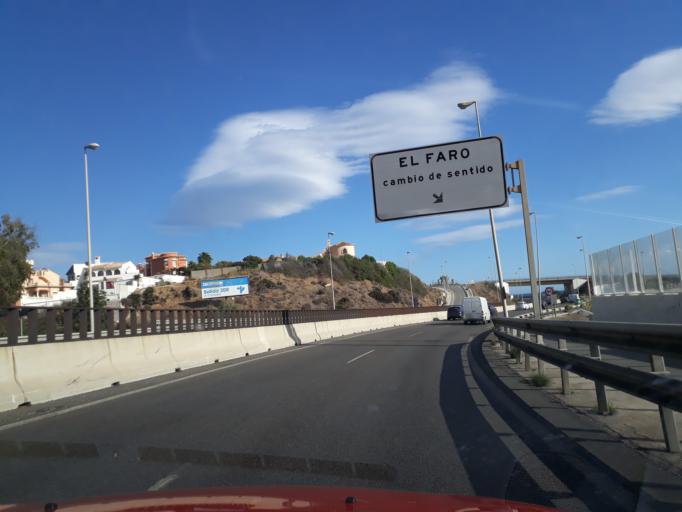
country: ES
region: Andalusia
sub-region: Provincia de Malaga
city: Fuengirola
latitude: 36.5080
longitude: -4.6460
